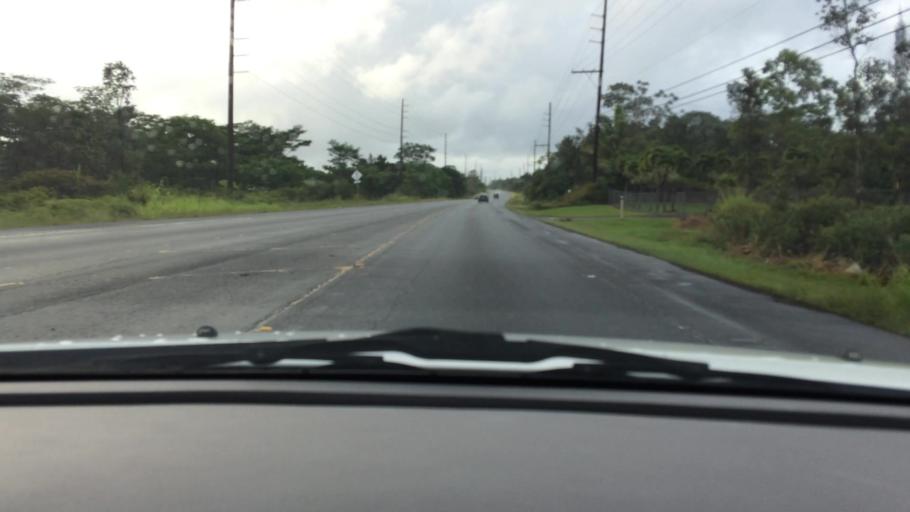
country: US
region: Hawaii
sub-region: Hawaii County
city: Ainaloa
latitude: 19.5525
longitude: -154.9847
